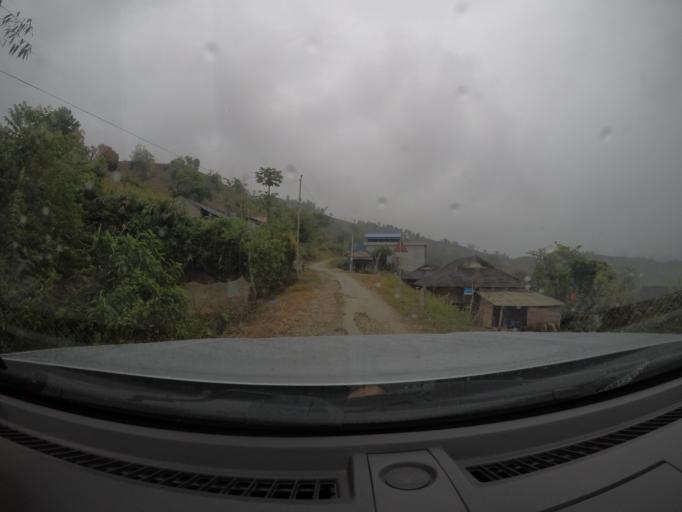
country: VN
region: Lai Chau
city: Tam Duong
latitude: 22.2724
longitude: 103.6585
